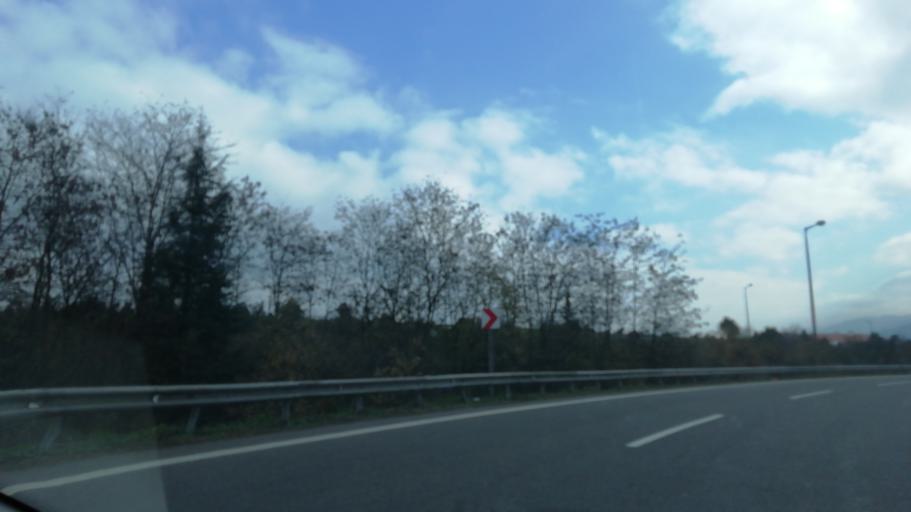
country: TR
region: Duzce
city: Kaynasli
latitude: 40.7863
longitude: 31.2753
